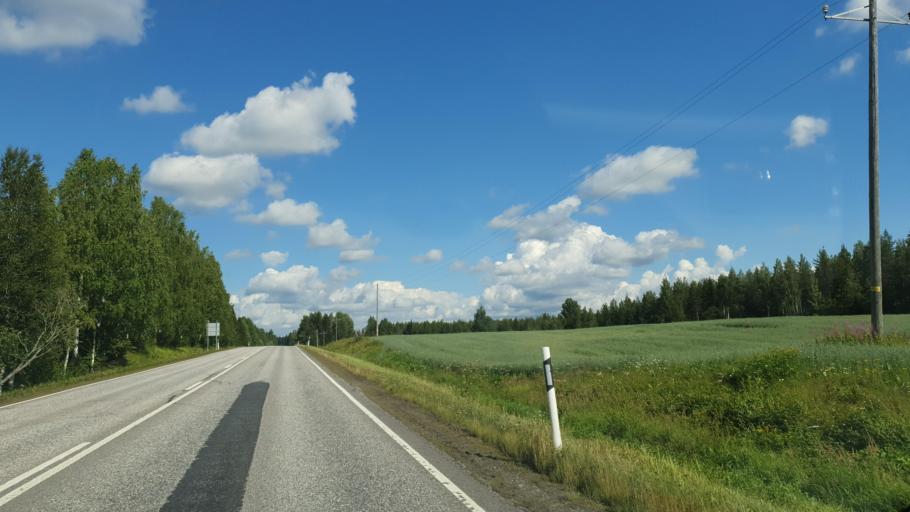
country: FI
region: Northern Savo
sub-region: Ylae-Savo
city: Sonkajaervi
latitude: 63.7293
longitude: 27.3750
